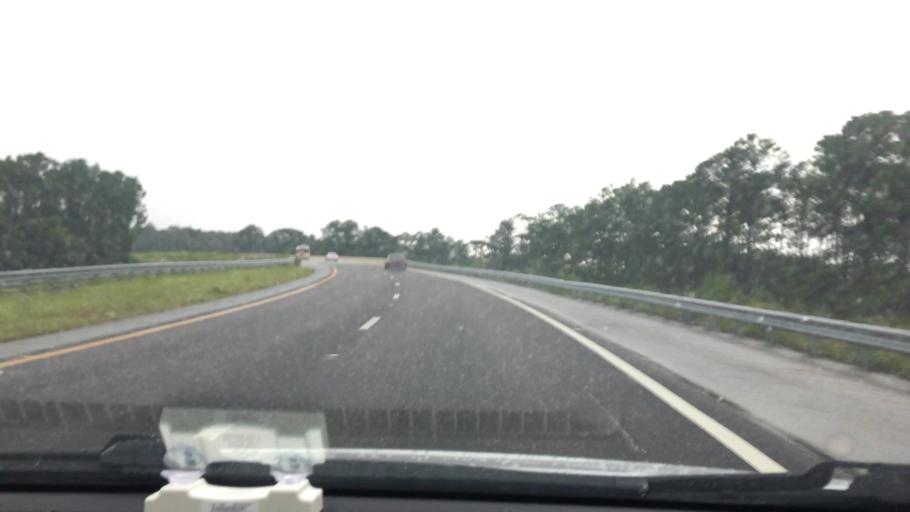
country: US
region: Florida
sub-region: Volusia County
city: Samsula-Spruce Creek
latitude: 29.1459
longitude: -81.1177
